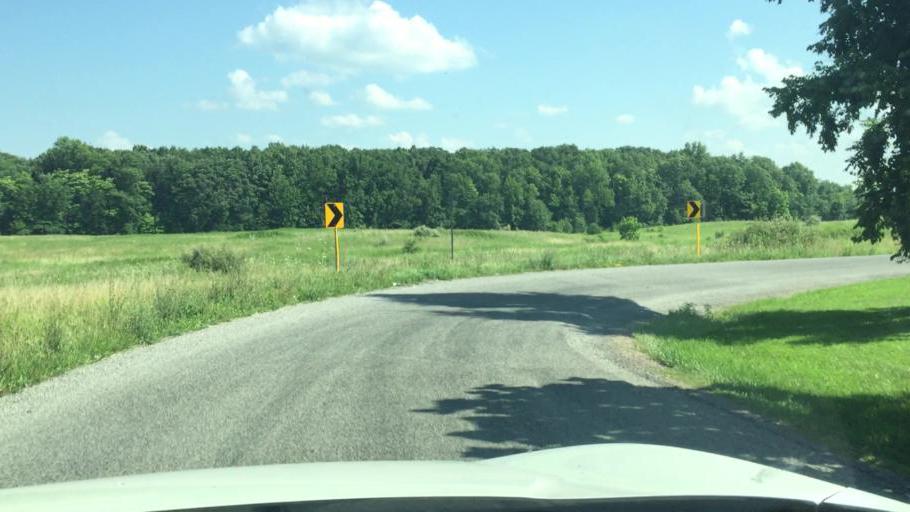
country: US
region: Ohio
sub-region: Champaign County
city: North Lewisburg
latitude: 40.2519
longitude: -83.5155
